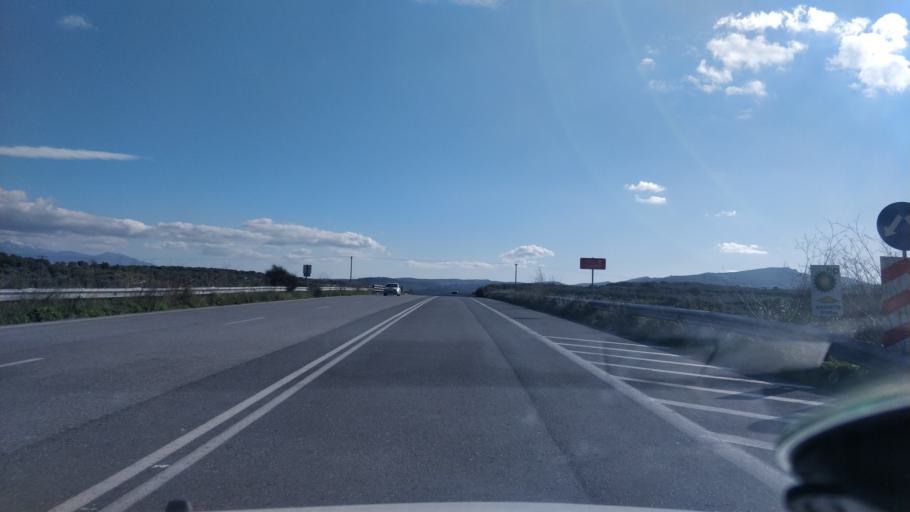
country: GR
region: Crete
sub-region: Nomos Irakleiou
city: Ano Arhanes
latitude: 35.2304
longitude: 25.1806
